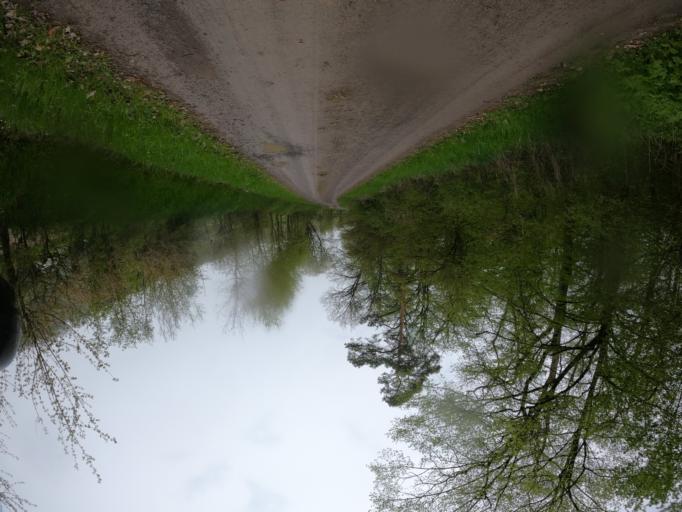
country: DE
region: Baden-Wuerttemberg
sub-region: Karlsruhe Region
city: Illingen
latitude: 48.9811
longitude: 8.8899
